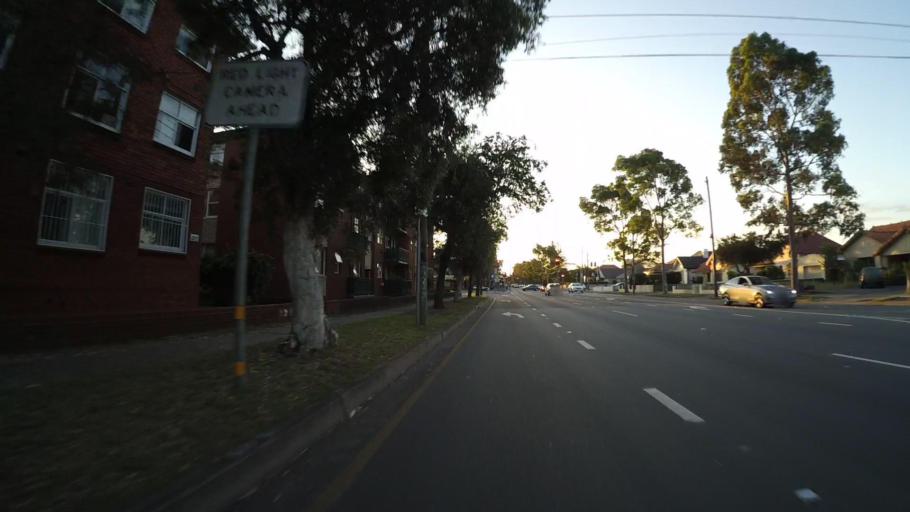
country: AU
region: New South Wales
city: Alexandria
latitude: -33.9232
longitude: 151.2080
